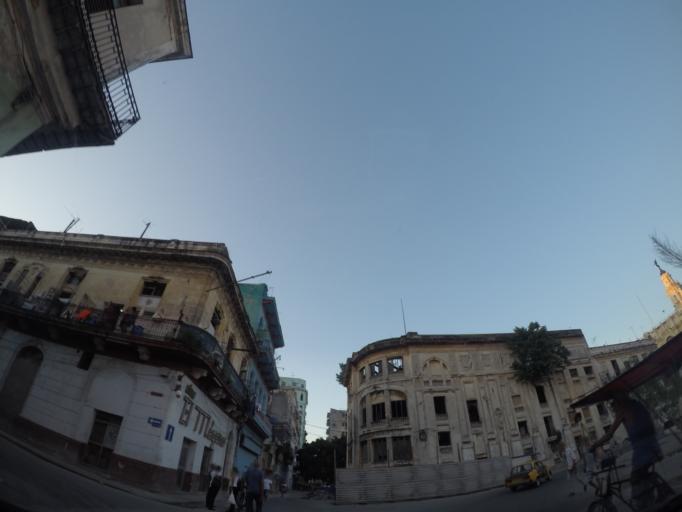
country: CU
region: La Habana
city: Centro Habana
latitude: 23.1361
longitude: -82.3606
